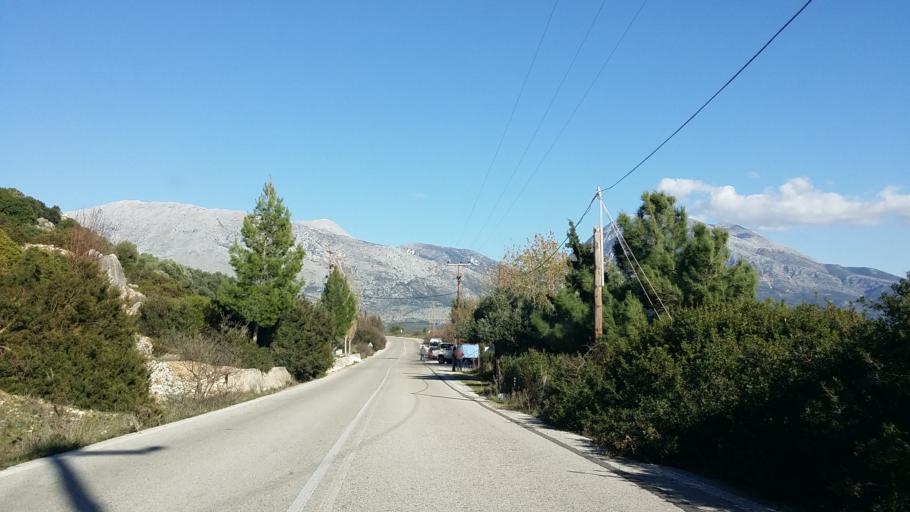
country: GR
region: West Greece
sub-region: Nomos Aitolias kai Akarnanias
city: Kandila
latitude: 38.6733
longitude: 20.9263
